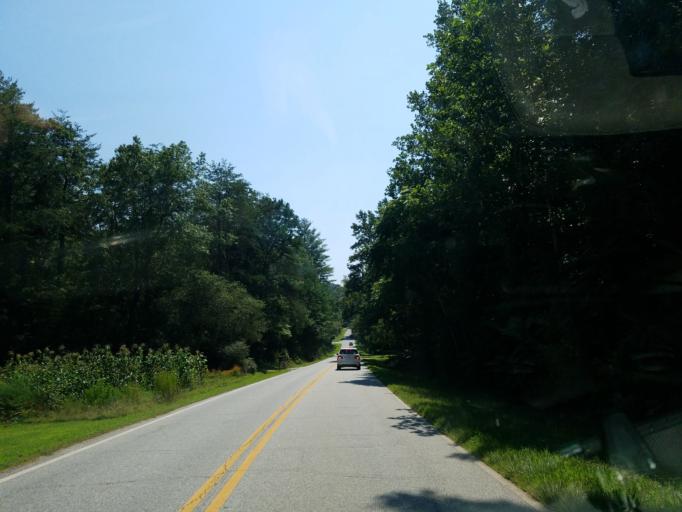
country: US
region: Georgia
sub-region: Lumpkin County
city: Dahlonega
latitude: 34.6392
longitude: -83.9136
